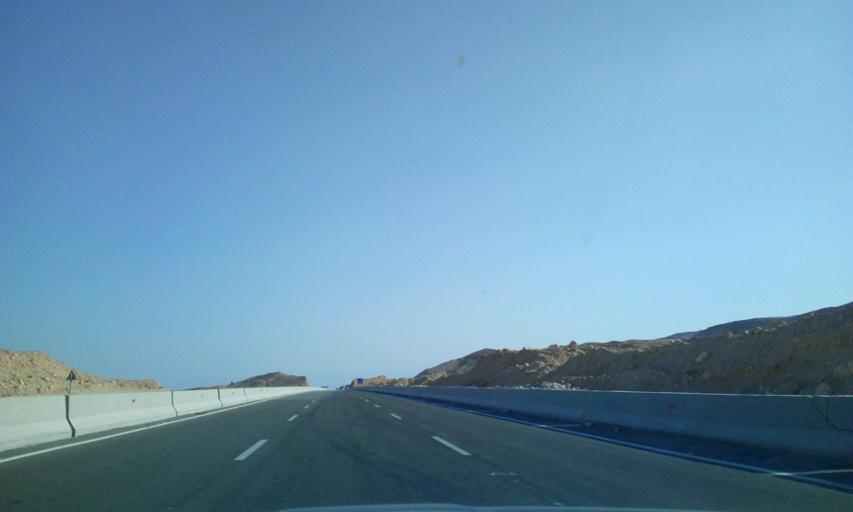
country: EG
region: As Suways
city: Ain Sukhna
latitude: 29.3006
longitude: 32.4662
